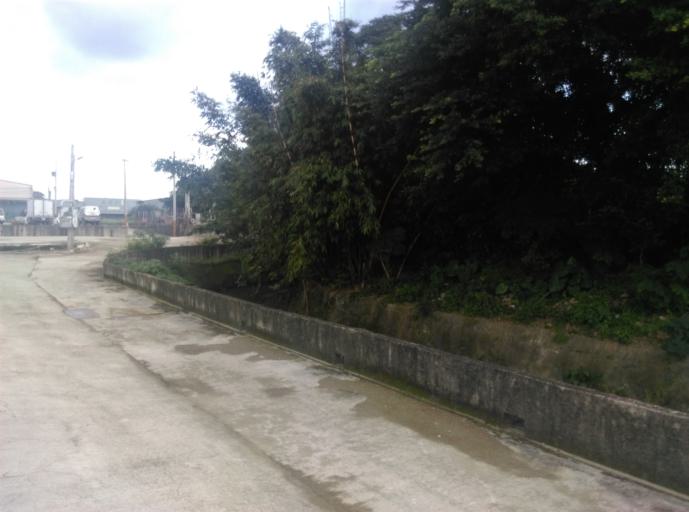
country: TW
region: Taiwan
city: Taoyuan City
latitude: 24.9937
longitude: 121.2516
